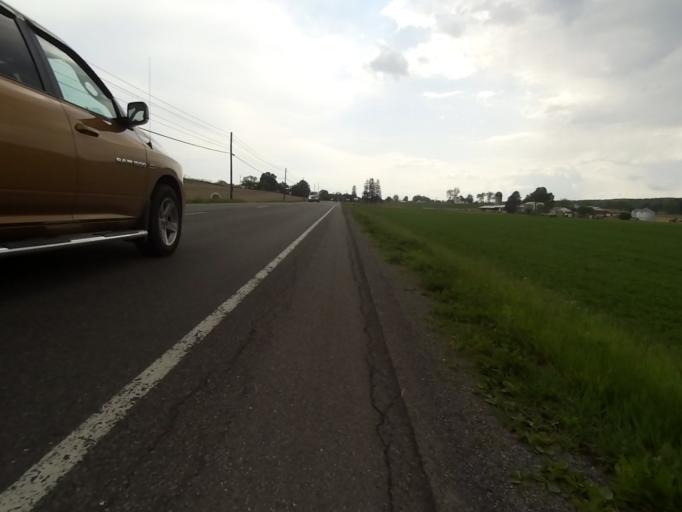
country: US
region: Pennsylvania
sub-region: Centre County
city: Zion
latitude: 40.9497
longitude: -77.6284
